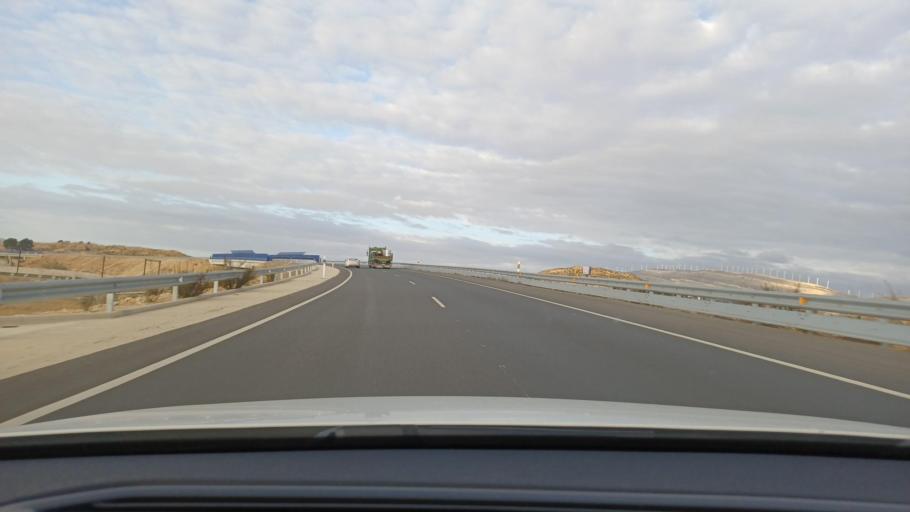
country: ES
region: Castille-La Mancha
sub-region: Provincia de Albacete
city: Caudete
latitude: 38.7305
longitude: -0.9330
